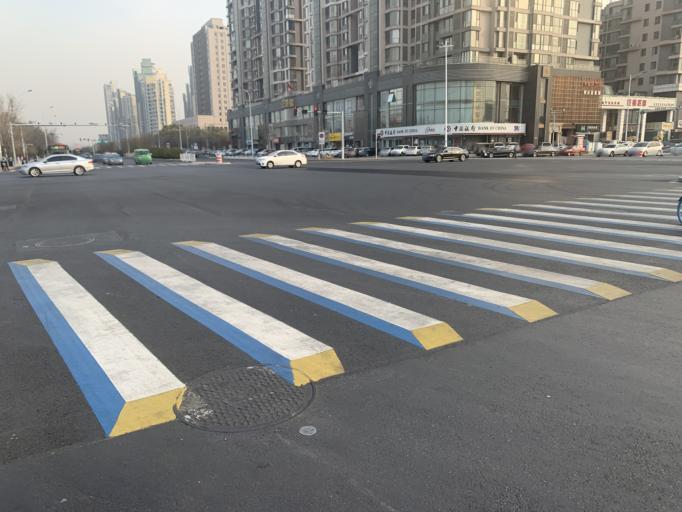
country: CN
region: Tianjin Shi
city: Liqizhuang
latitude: 39.0792
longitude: 117.1519
